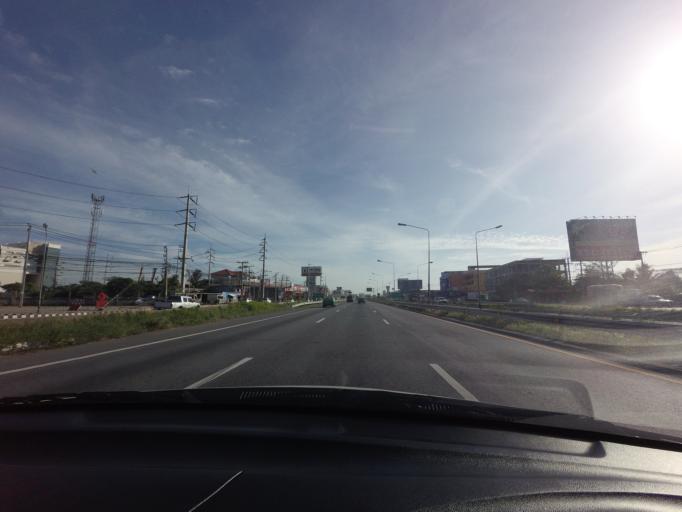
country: TH
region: Nonthaburi
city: Bang Bua Thong
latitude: 13.9259
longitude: 100.4134
